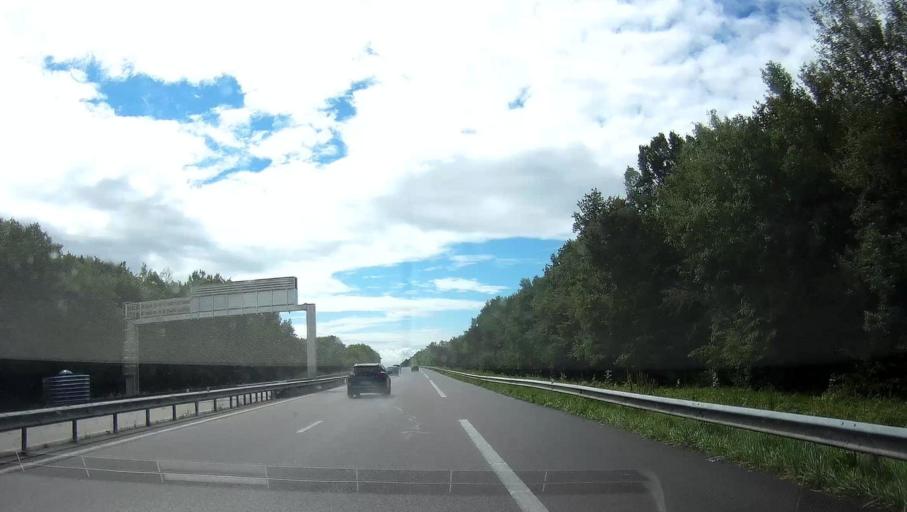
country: FR
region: Champagne-Ardenne
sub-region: Departement de l'Aube
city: Verrieres
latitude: 48.2663
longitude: 4.1645
